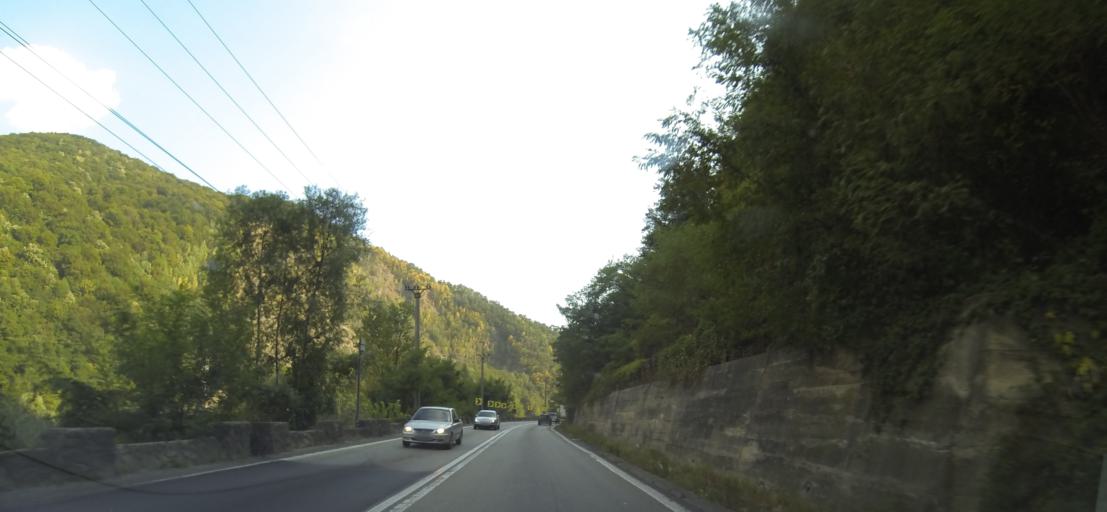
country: RO
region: Valcea
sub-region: Comuna Brezoi
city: Brezoi
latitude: 45.3077
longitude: 24.2882
